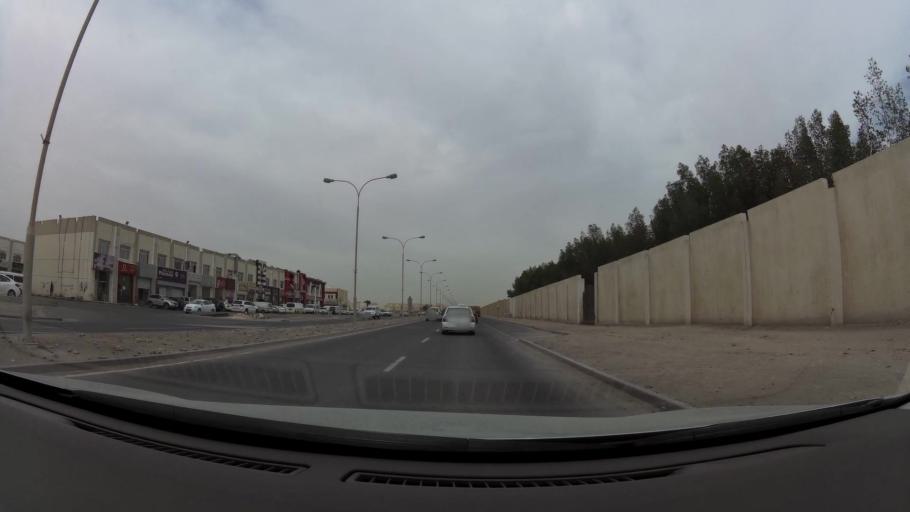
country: QA
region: Baladiyat ar Rayyan
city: Ar Rayyan
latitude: 25.2241
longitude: 51.4507
